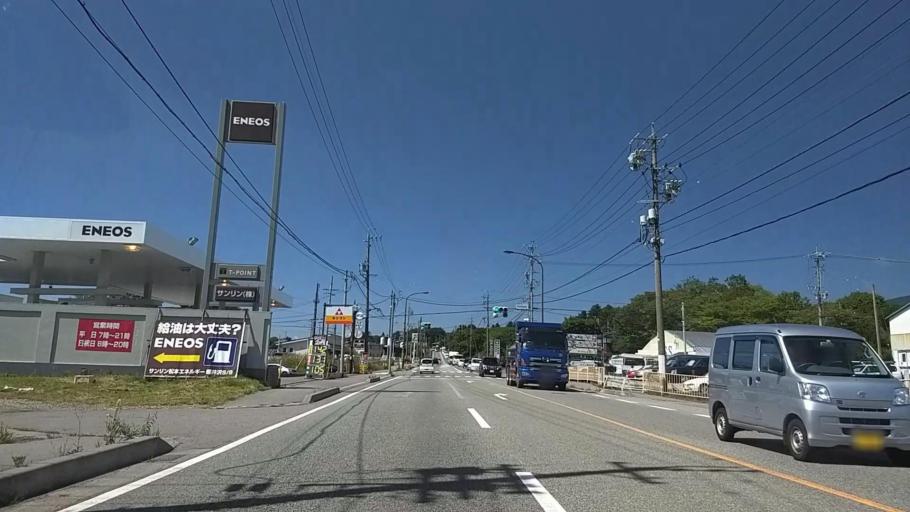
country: JP
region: Nagano
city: Komoro
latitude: 36.3434
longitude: 138.5639
